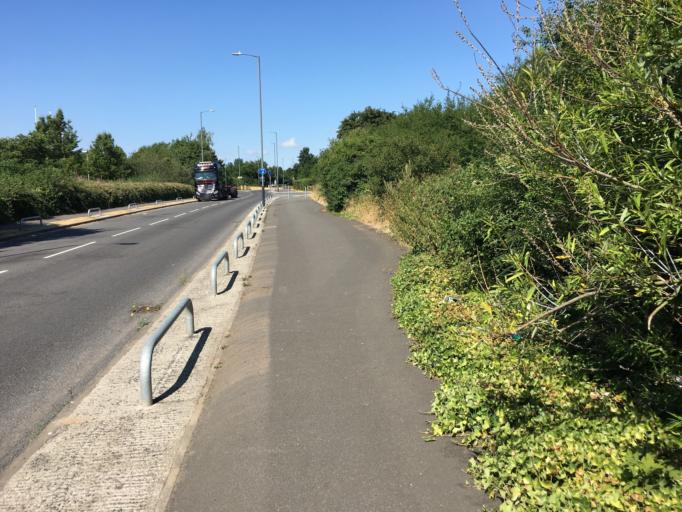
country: GB
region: England
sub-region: Warwickshire
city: Rugby
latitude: 52.4023
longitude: -1.2415
